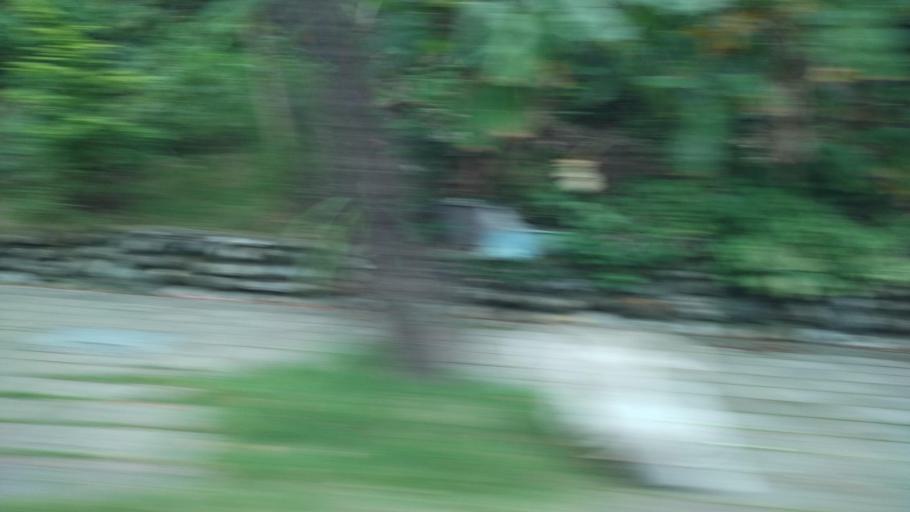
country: TW
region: Taiwan
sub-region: Hualien
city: Hualian
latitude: 23.9962
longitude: 121.6216
